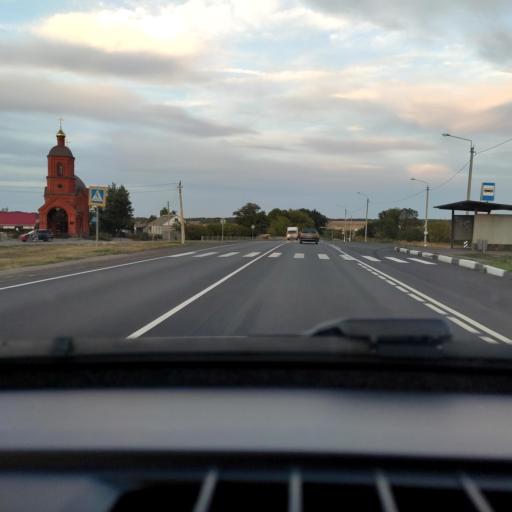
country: RU
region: Voronezj
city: Panino
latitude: 51.4854
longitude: 40.1969
